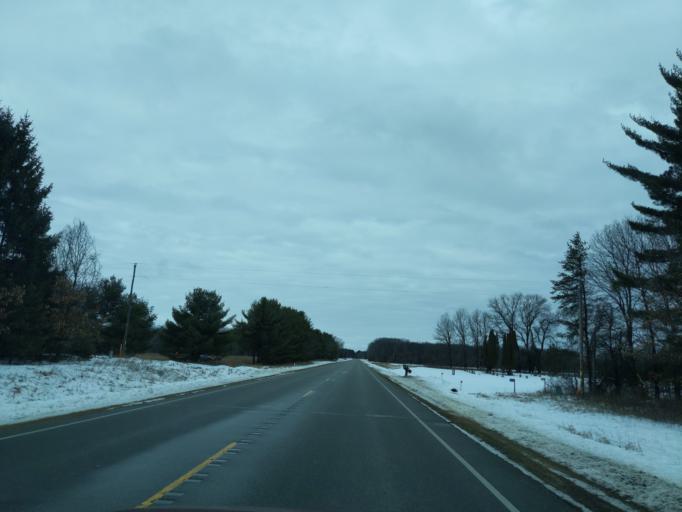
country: US
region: Wisconsin
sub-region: Marquette County
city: Montello
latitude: 43.9264
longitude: -89.3122
